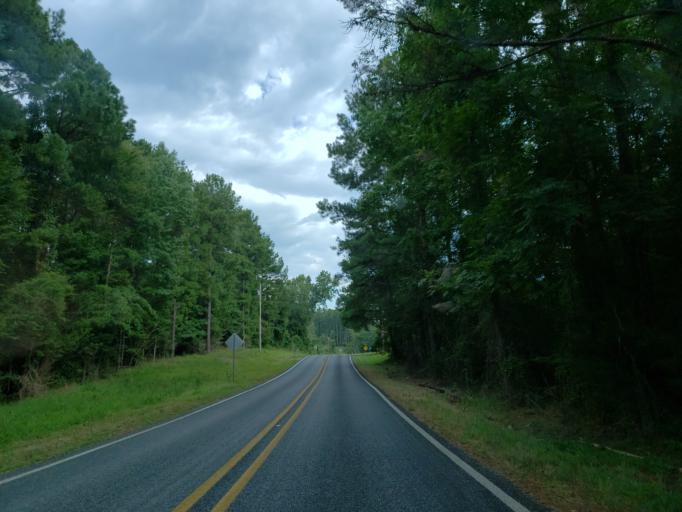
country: US
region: Mississippi
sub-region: Clarke County
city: Stonewall
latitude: 32.1762
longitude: -88.9150
